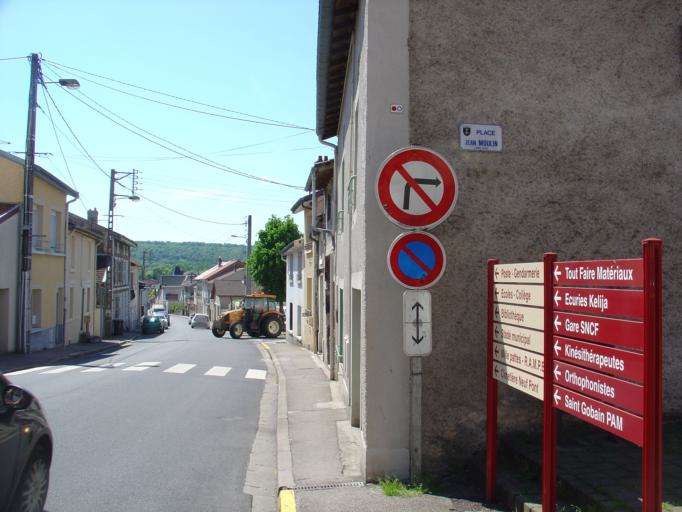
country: FR
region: Lorraine
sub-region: Departement de Meurthe-et-Moselle
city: Foug
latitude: 48.6838
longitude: 5.7891
